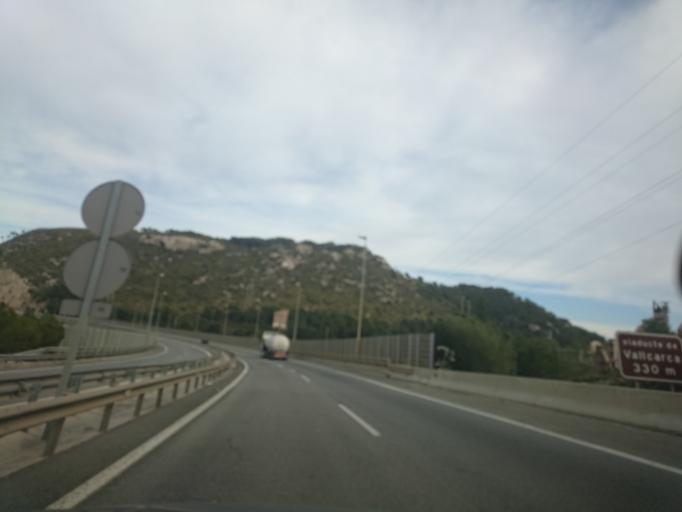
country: ES
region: Catalonia
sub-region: Provincia de Barcelona
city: Sitges
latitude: 41.2439
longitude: 1.8579
